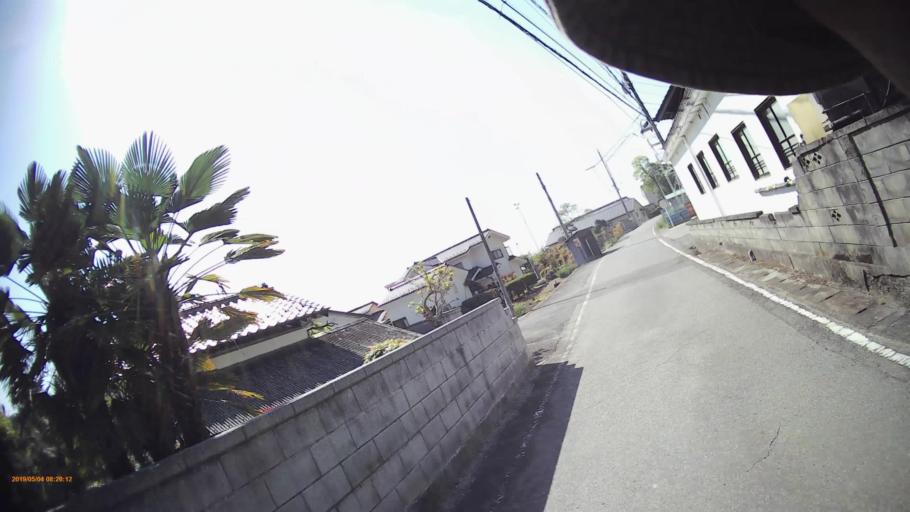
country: JP
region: Yamanashi
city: Nirasaki
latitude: 35.7341
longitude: 138.4090
